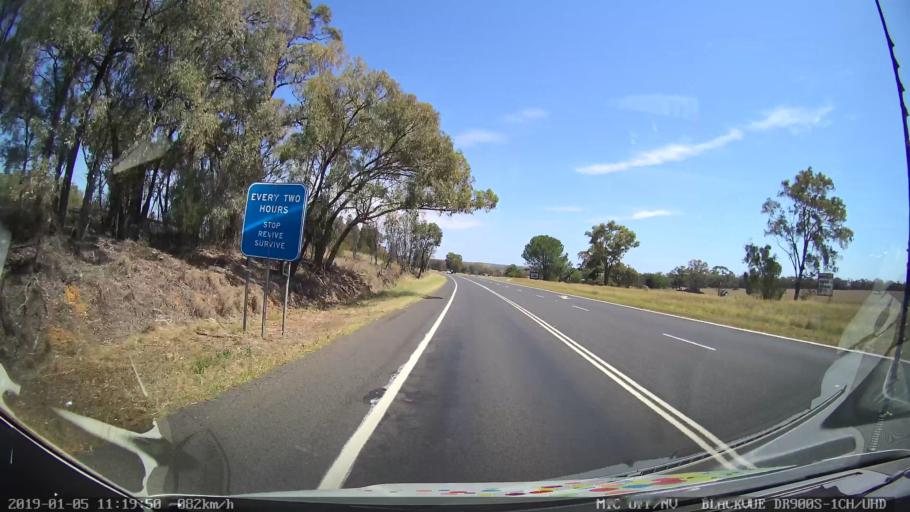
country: AU
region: New South Wales
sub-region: Warrumbungle Shire
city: Coonabarabran
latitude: -31.2992
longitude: 149.2938
